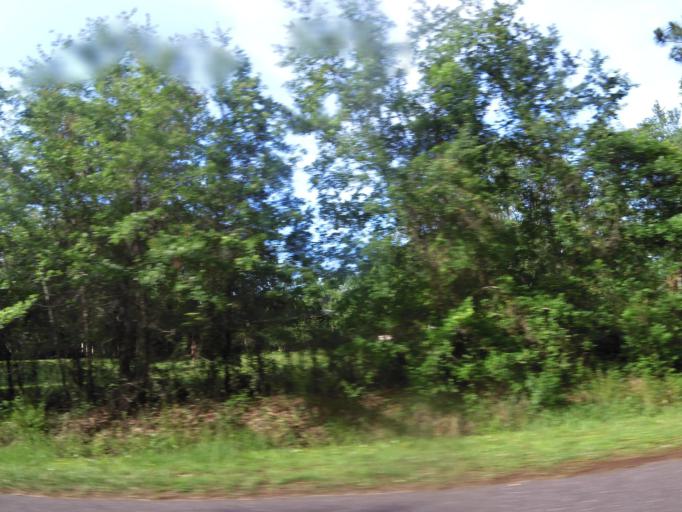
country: US
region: Florida
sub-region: Nassau County
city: Fernandina Beach
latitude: 30.5121
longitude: -81.4847
